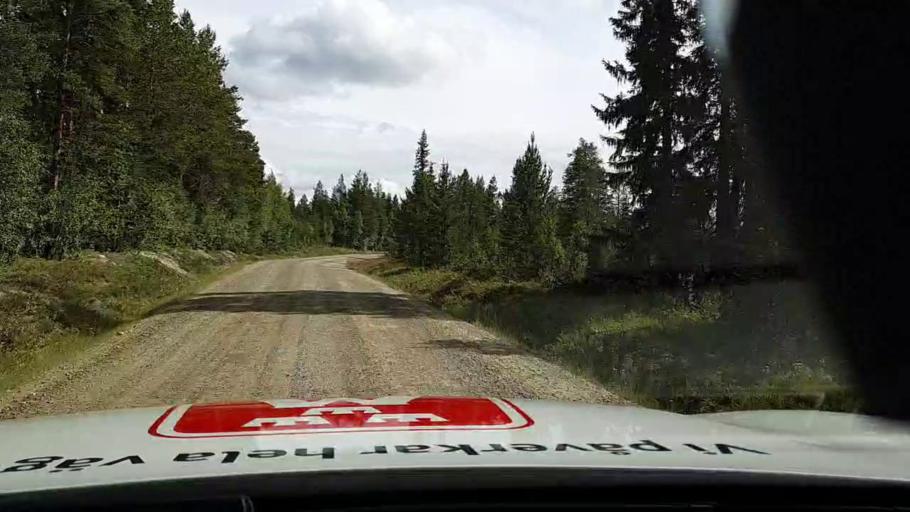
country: SE
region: Jaemtland
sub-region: Are Kommun
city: Jarpen
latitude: 62.5450
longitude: 13.4725
